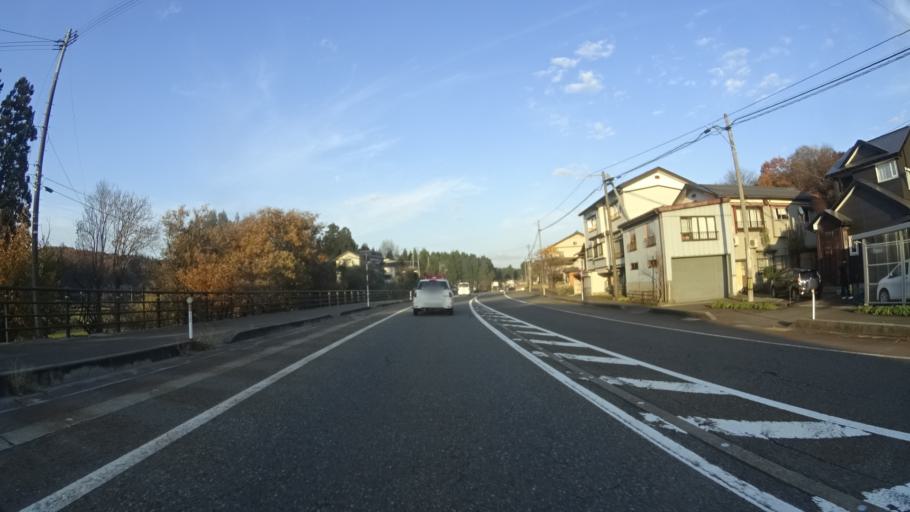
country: JP
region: Niigata
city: Nagaoka
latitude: 37.4345
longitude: 138.7289
